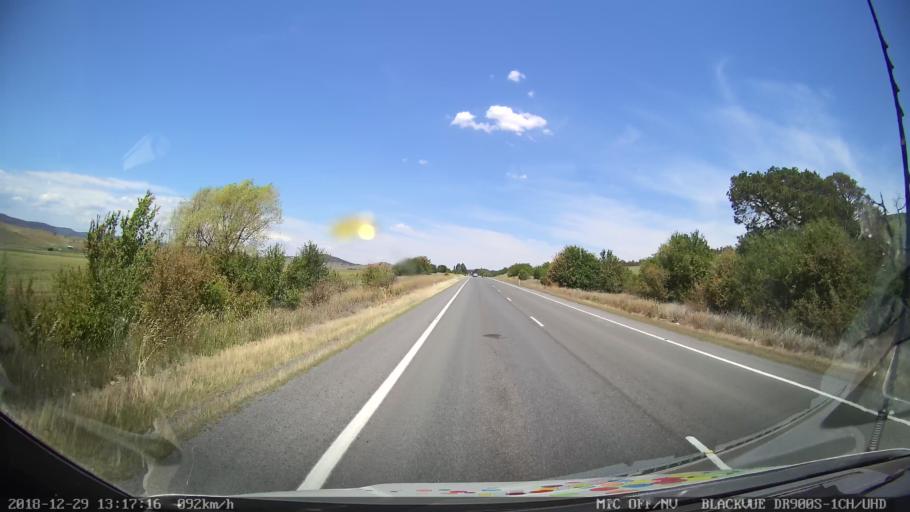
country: AU
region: Australian Capital Territory
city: Macarthur
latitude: -35.7351
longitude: 149.1608
